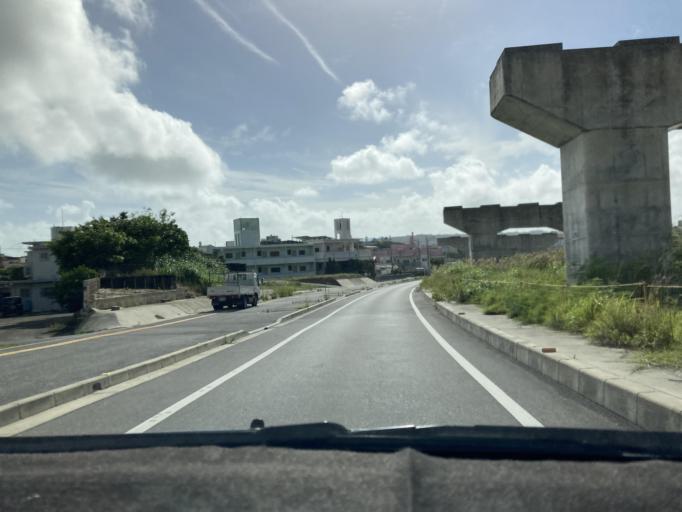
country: JP
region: Okinawa
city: Naha-shi
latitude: 26.2055
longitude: 127.7329
